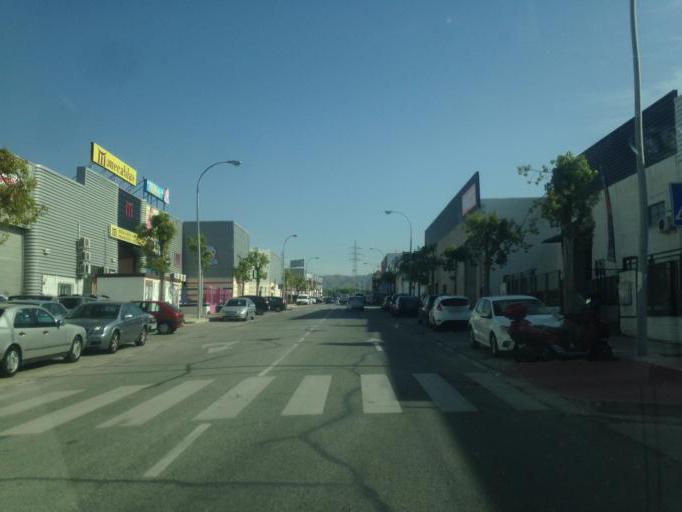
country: ES
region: Andalusia
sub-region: Provincia de Malaga
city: Malaga
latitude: 36.7089
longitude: -4.4691
